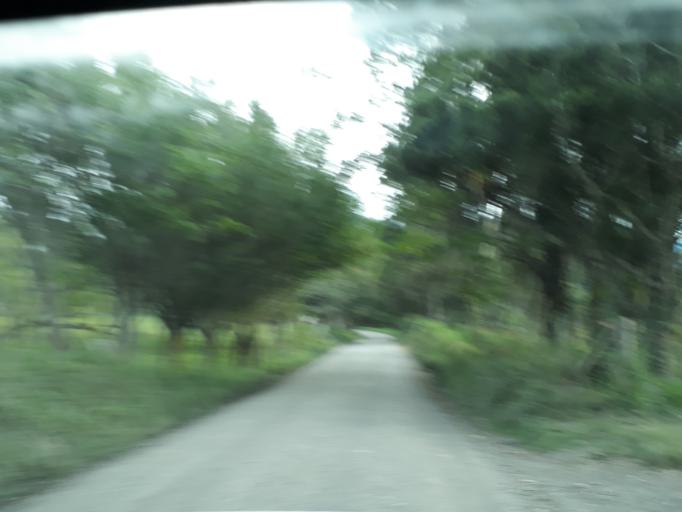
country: CO
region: Cundinamarca
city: Pacho
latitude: 5.1645
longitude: -74.1246
